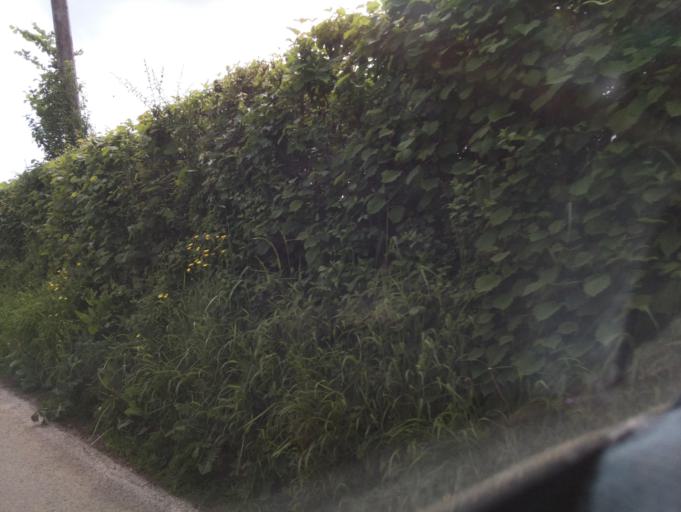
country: GB
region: England
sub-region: Herefordshire
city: Llanrothal
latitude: 51.8749
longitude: -2.8072
